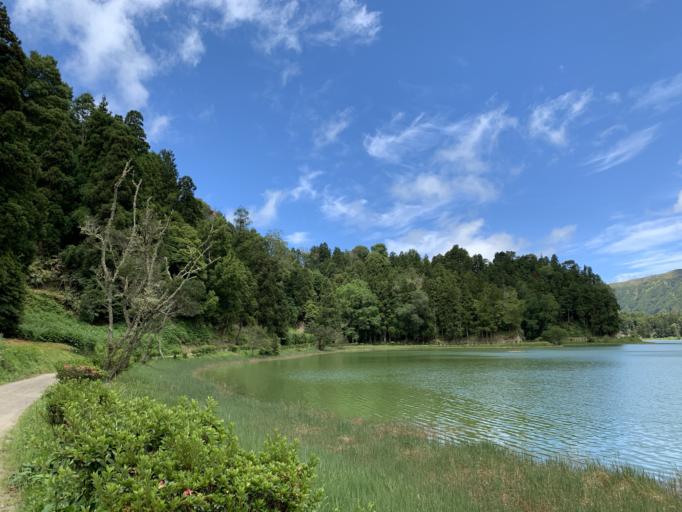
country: PT
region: Azores
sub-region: Ponta Delgada
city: Arrifes
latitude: 37.8478
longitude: -25.7936
